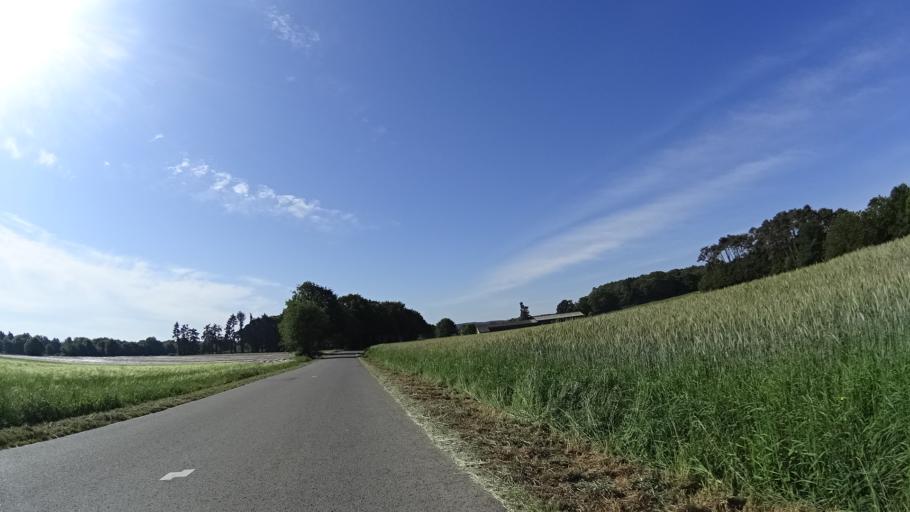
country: FR
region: Brittany
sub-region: Departement d'Ille-et-Vilaine
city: Guipry
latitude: 47.8100
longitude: -1.8498
